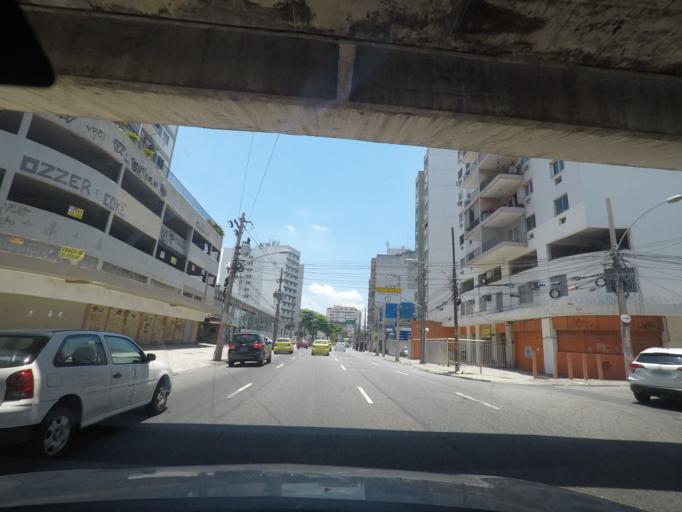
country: BR
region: Rio de Janeiro
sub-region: Rio De Janeiro
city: Rio de Janeiro
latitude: -22.9052
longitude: -43.2418
